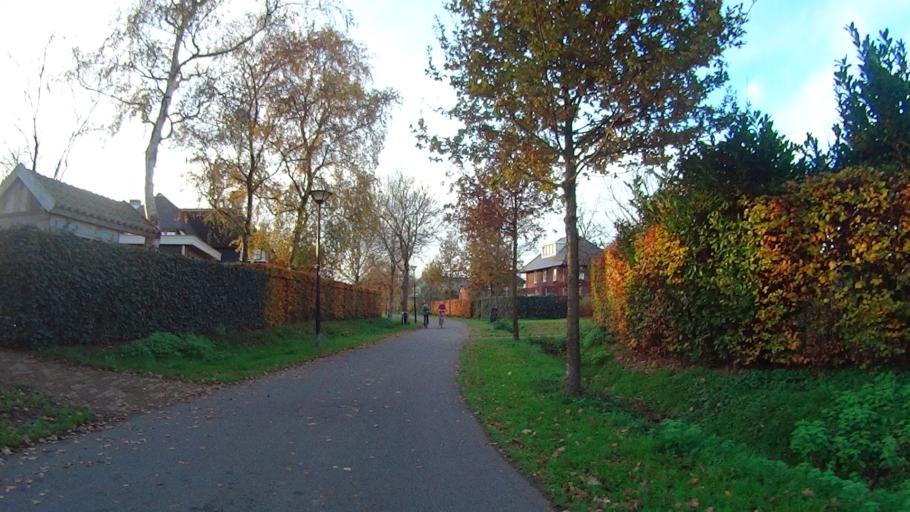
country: NL
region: Utrecht
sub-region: Gemeente Amersfoort
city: Hoogland
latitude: 52.1990
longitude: 5.4225
